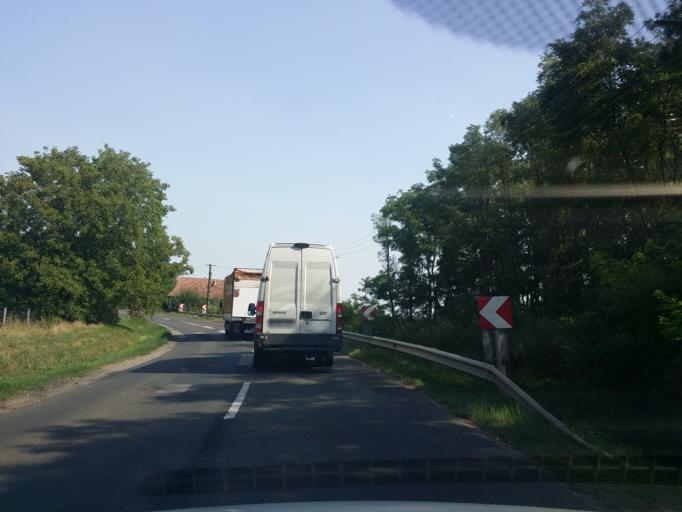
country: HU
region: Fejer
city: Mezofalva
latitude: 46.9345
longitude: 18.7533
